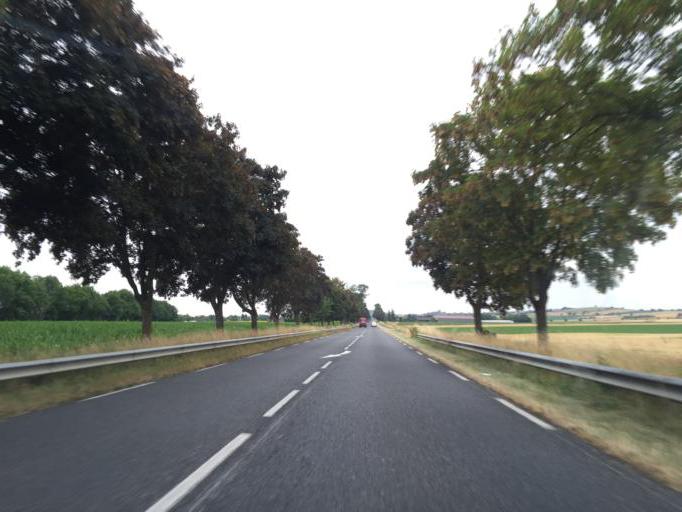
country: FR
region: Auvergne
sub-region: Departement de l'Allier
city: Gannat
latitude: 46.1469
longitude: 3.2216
